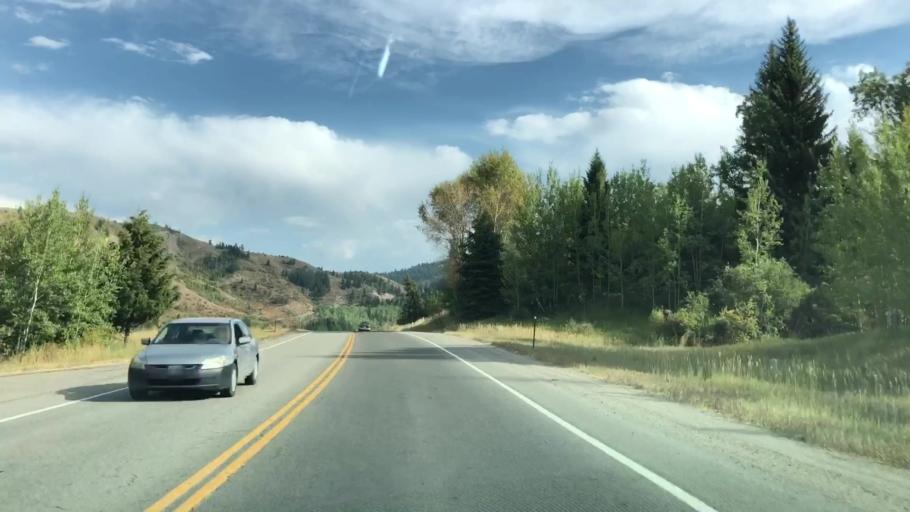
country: US
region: Wyoming
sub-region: Teton County
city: South Park
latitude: 43.3588
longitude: -110.7250
